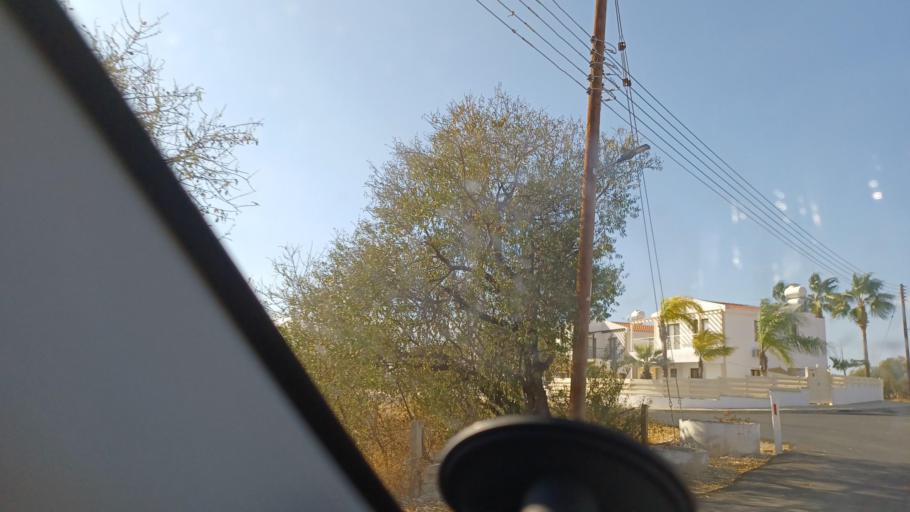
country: CY
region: Pafos
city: Mesogi
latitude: 34.7358
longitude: 32.5365
